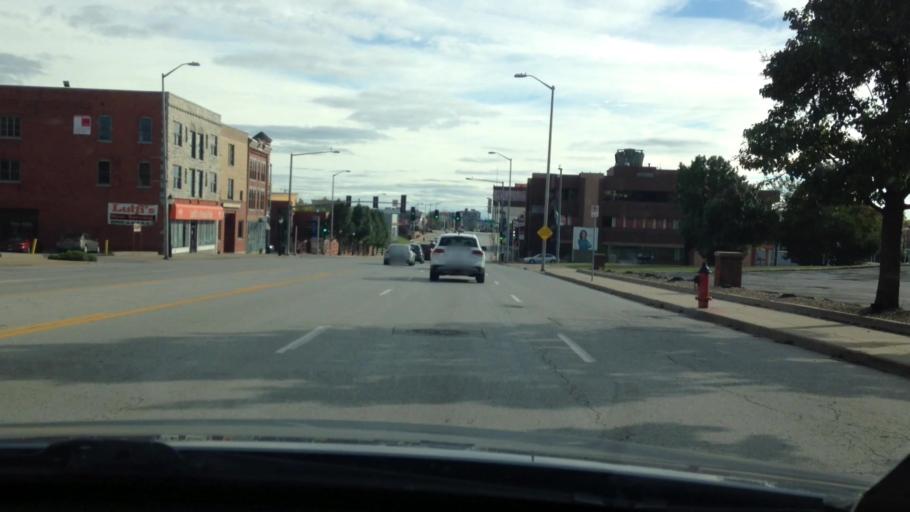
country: US
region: Missouri
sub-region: Jackson County
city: Kansas City
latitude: 39.0720
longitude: -94.5853
